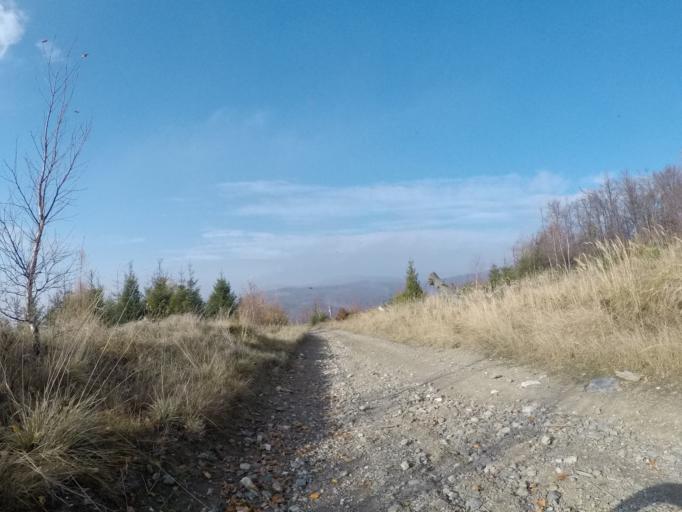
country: SK
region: Kosicky
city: Gelnica
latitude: 48.7602
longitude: 21.0407
